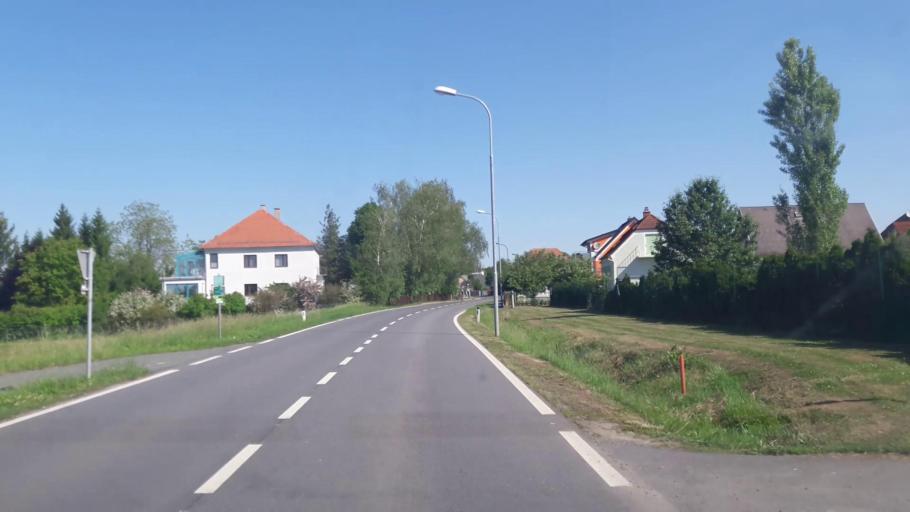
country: AT
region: Burgenland
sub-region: Politischer Bezirk Jennersdorf
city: Deutsch Kaltenbrunn
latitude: 47.0808
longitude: 16.1096
